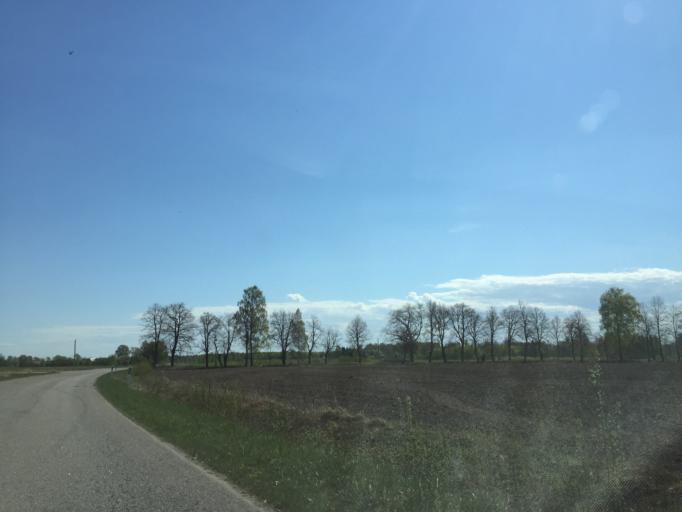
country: LV
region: Saulkrastu
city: Saulkrasti
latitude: 57.3300
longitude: 24.4642
